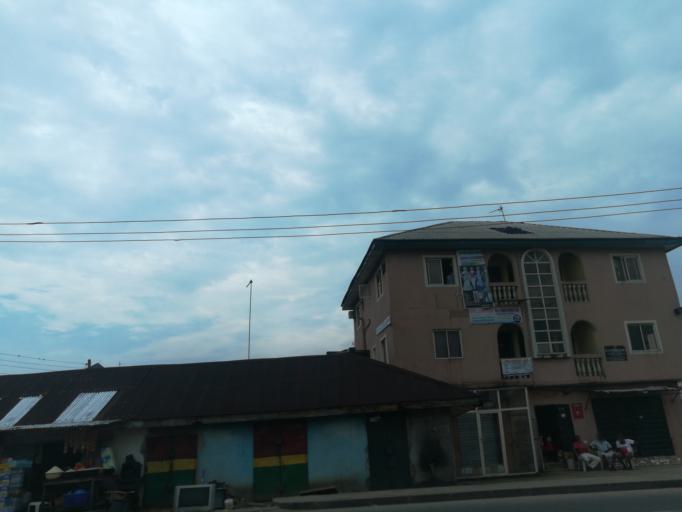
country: NG
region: Rivers
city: Port Harcourt
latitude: 4.8496
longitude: 6.9785
